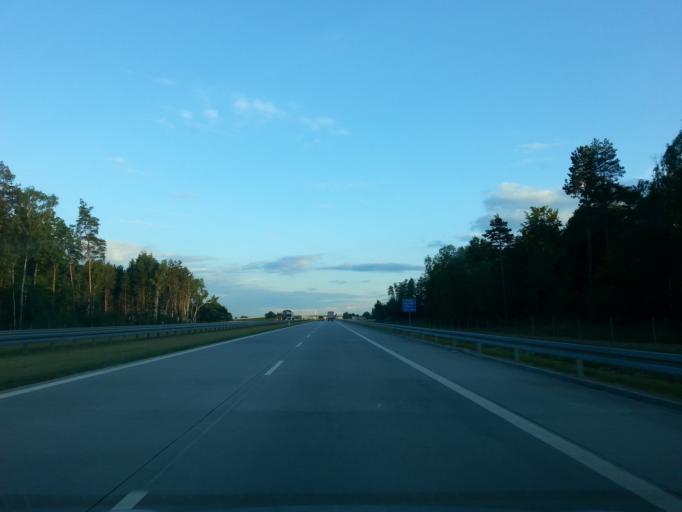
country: PL
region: Lodz Voivodeship
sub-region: Powiat sieradzki
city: Zloczew
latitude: 51.4360
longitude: 18.6457
